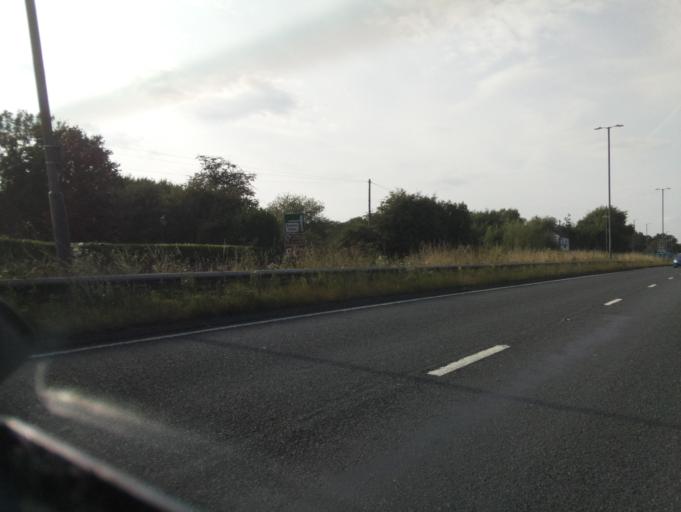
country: GB
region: England
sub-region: Solihull
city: Tidbury Green
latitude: 52.3512
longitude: -1.8825
